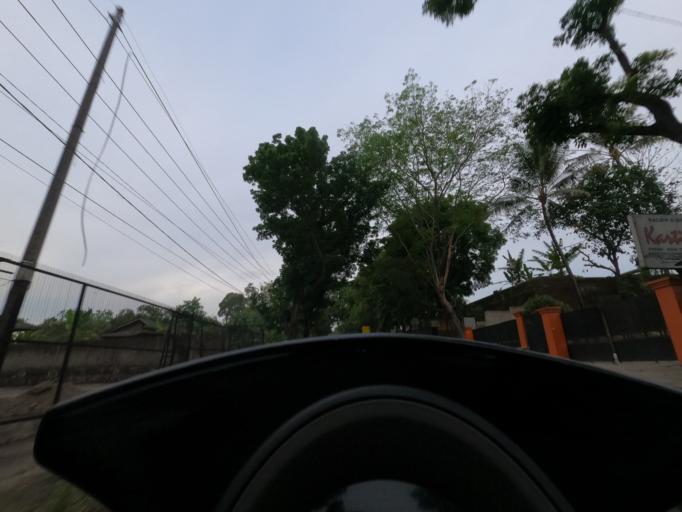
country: ID
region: West Java
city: Lembang
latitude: -6.5829
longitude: 107.7443
